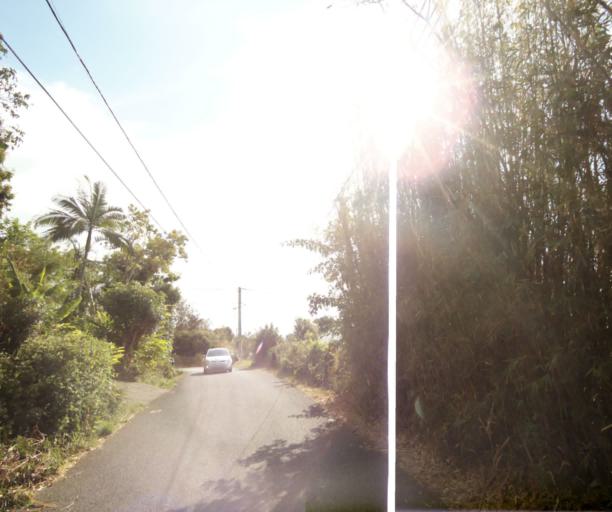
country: RE
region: Reunion
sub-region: Reunion
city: Saint-Paul
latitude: -20.9987
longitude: 55.3333
